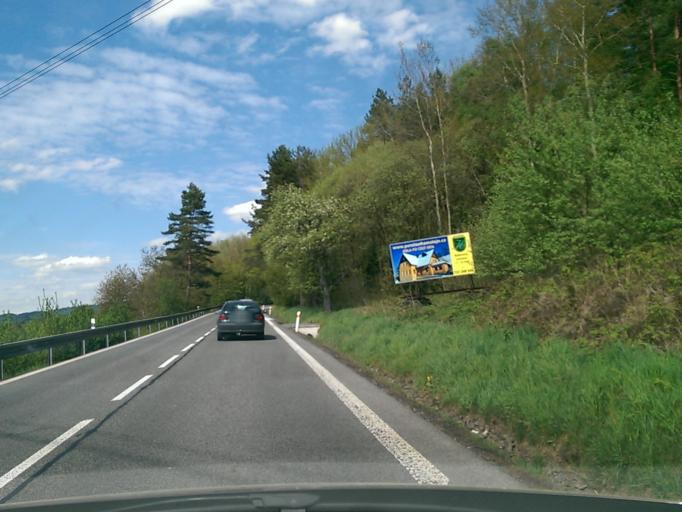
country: CZ
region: Liberecky
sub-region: Okres Semily
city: Turnov
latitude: 50.6143
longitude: 15.1650
